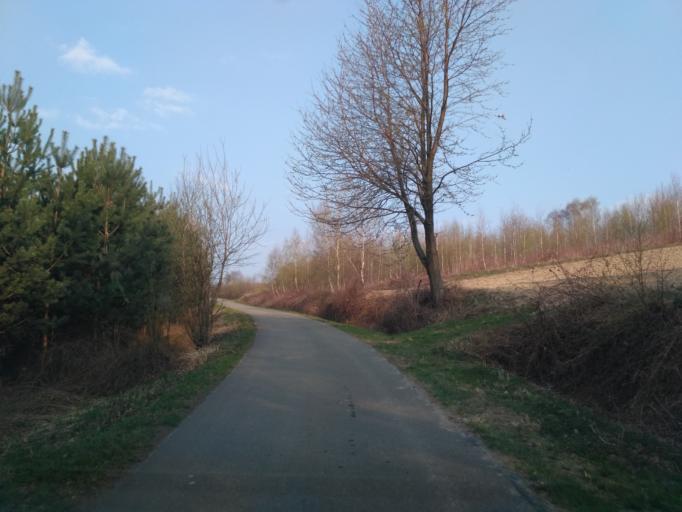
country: PL
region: Subcarpathian Voivodeship
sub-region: Powiat strzyzowski
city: Wisniowa
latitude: 49.8887
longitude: 21.6272
